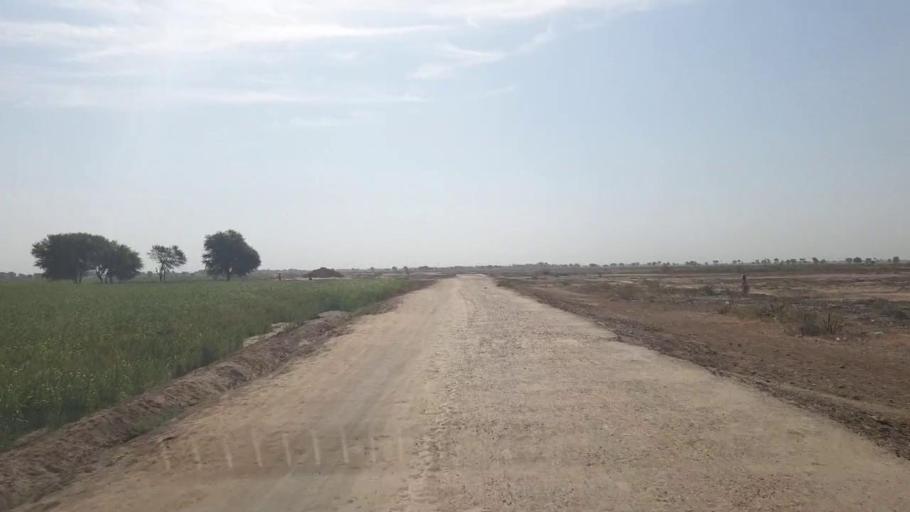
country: PK
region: Sindh
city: Umarkot
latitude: 25.2873
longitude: 69.6538
